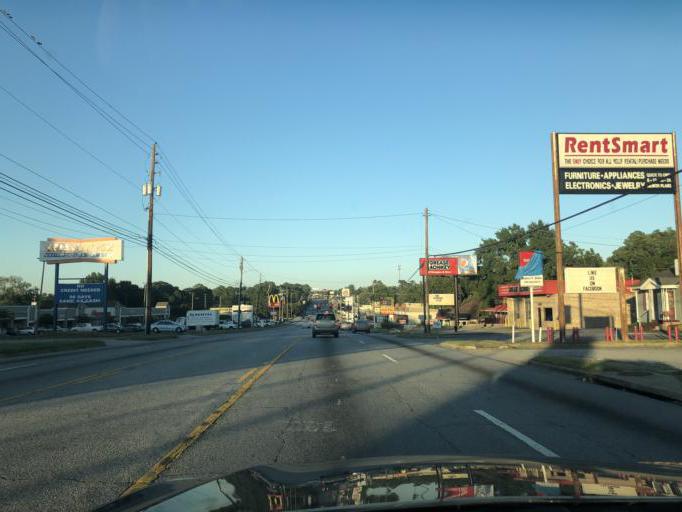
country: US
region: Georgia
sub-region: Muscogee County
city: Columbus
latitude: 32.4631
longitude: -84.9266
